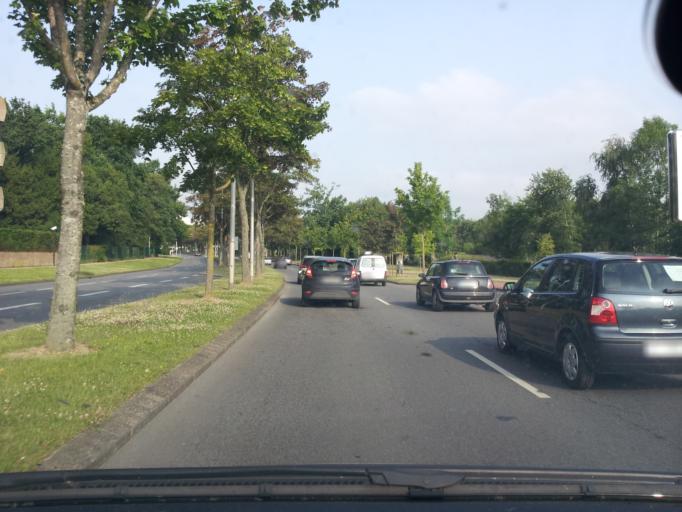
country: FR
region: Ile-de-France
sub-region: Departement de l'Essonne
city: Evry
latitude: 48.6245
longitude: 2.4395
